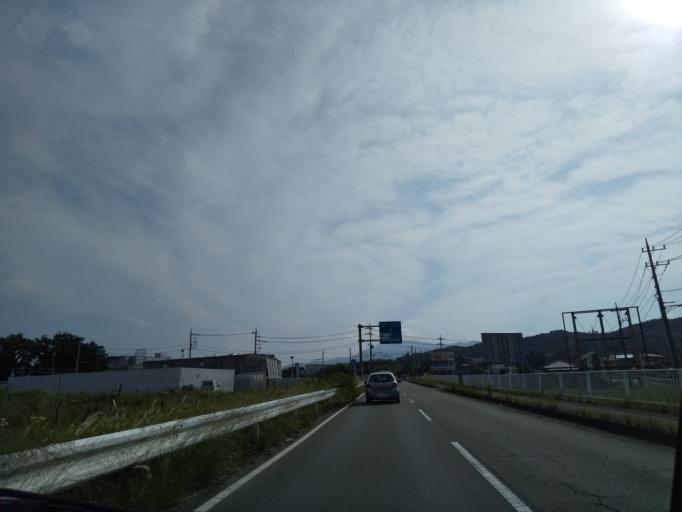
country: JP
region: Kanagawa
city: Zama
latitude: 35.4986
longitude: 139.3473
